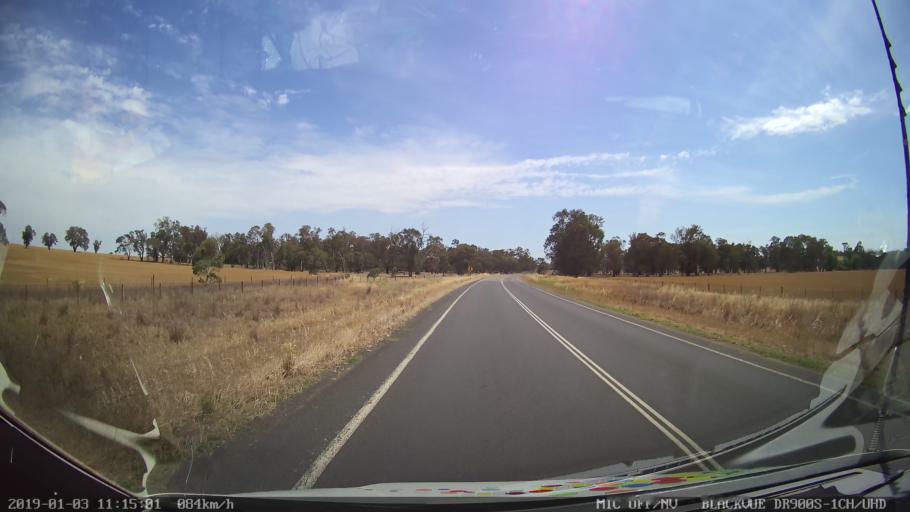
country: AU
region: New South Wales
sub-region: Young
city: Young
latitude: -34.1688
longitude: 148.2618
